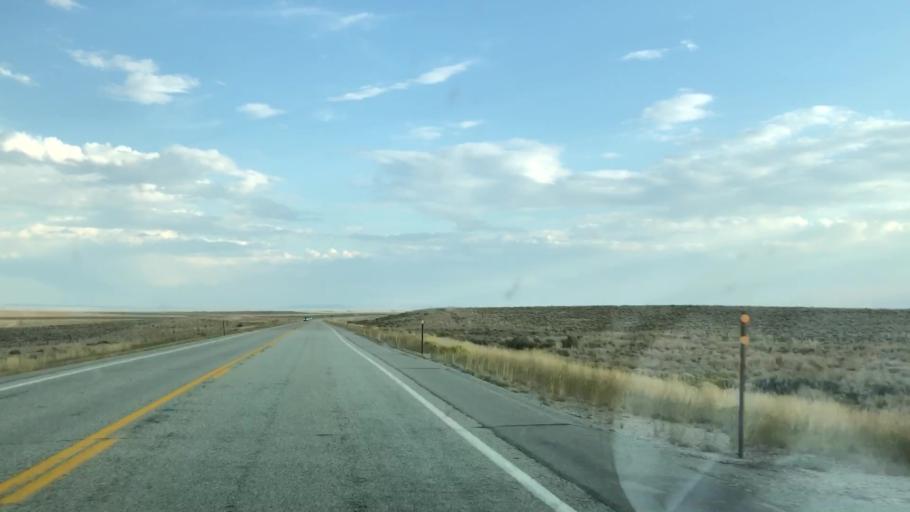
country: US
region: Wyoming
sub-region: Sweetwater County
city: North Rock Springs
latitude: 42.2618
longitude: -109.4728
